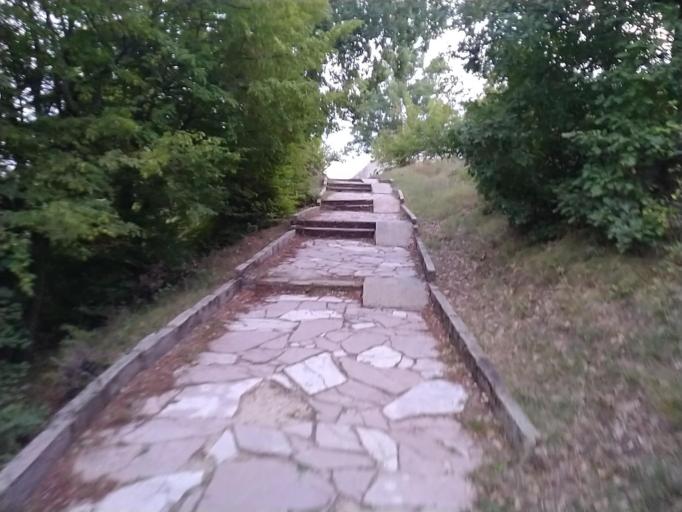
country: BG
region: Plovdiv
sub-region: Obshtina Khisarya
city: Khisarya
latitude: 42.4962
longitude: 24.7033
